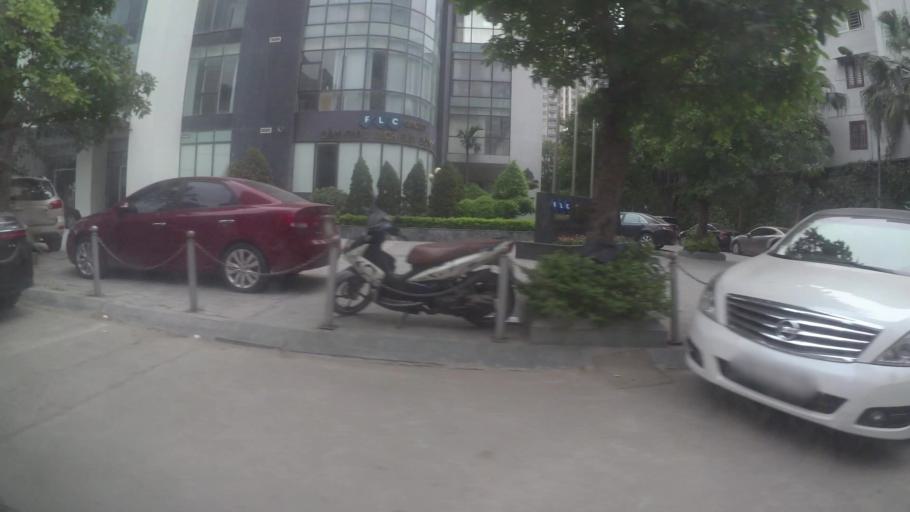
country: VN
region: Ha Noi
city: Cau Dien
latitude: 21.0352
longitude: 105.7715
